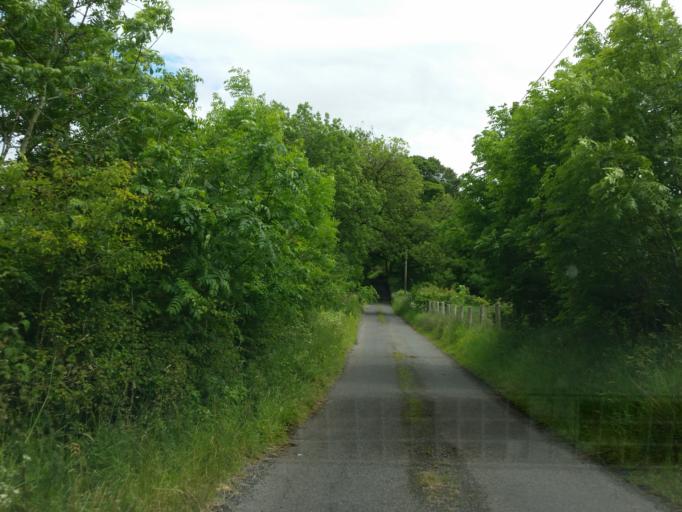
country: GB
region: Northern Ireland
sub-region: Omagh District
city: Omagh
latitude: 54.5579
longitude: -7.0756
